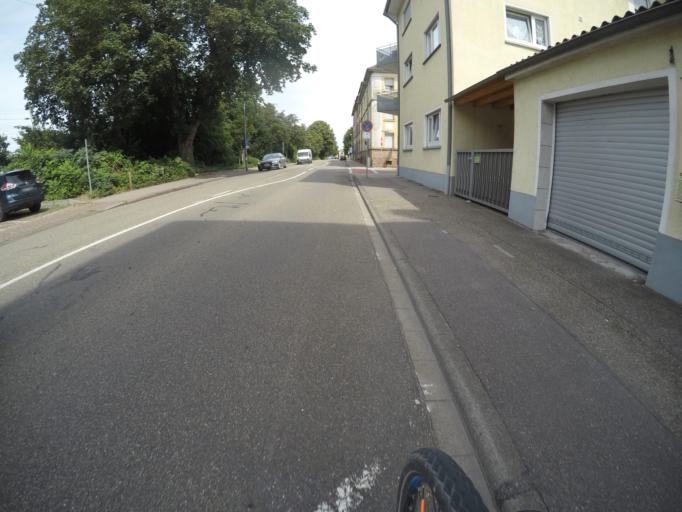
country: DE
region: Baden-Wuerttemberg
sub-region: Karlsruhe Region
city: Bruchsal
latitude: 49.1283
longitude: 8.5925
